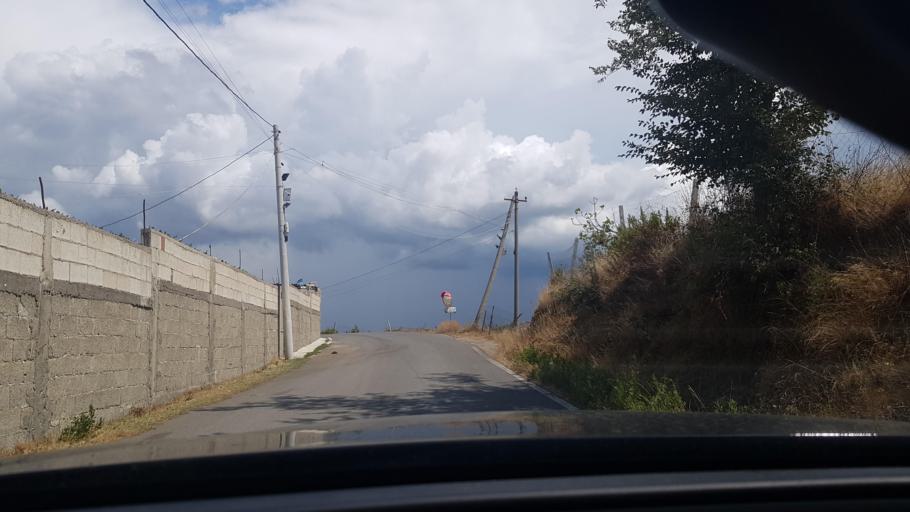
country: AL
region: Durres
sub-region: Rrethi i Durresit
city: Rrashbull
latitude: 41.2917
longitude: 19.5376
